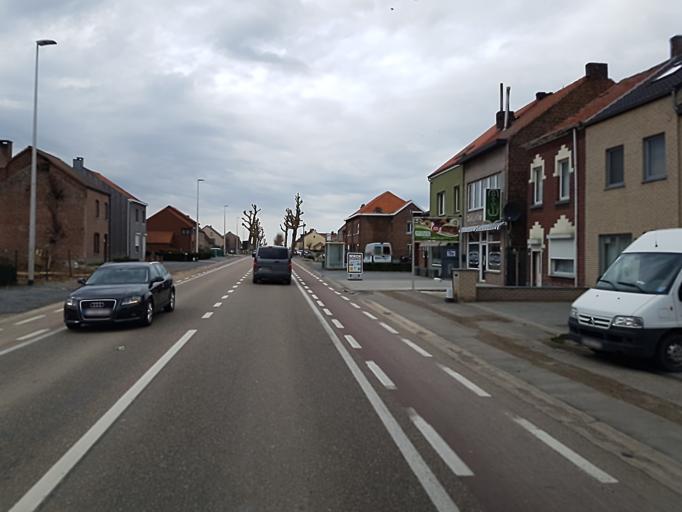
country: BE
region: Flanders
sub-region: Provincie Limburg
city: Heers
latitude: 50.8067
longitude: 5.2862
